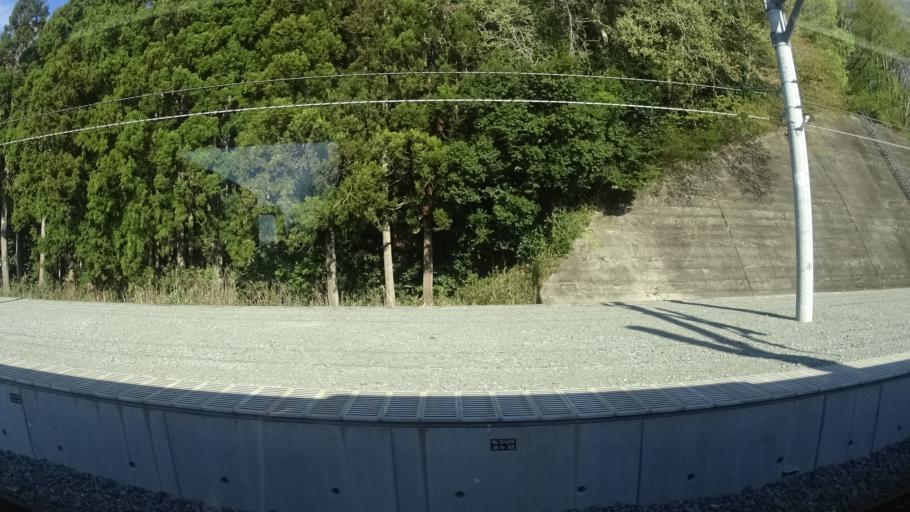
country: JP
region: Fukushima
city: Namie
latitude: 37.5299
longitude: 140.9850
